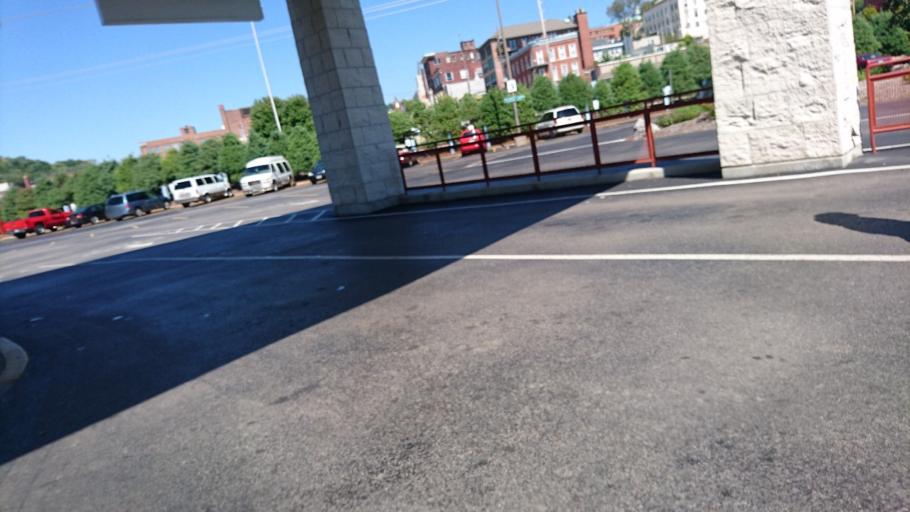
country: US
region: Illinois
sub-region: Madison County
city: Alton
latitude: 38.8888
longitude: -90.1859
